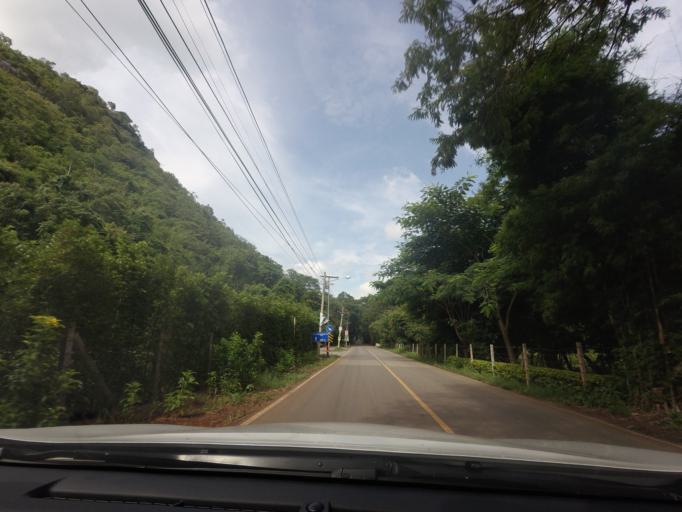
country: TH
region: Nakhon Ratchasima
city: Pak Chong
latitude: 14.5472
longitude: 101.4180
